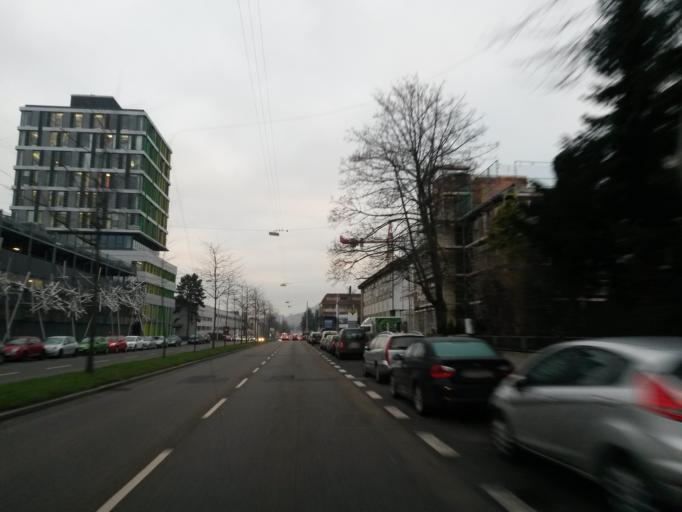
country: DE
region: Baden-Wuerttemberg
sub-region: Regierungsbezirk Stuttgart
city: Heilbronn
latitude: 49.1360
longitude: 9.2292
